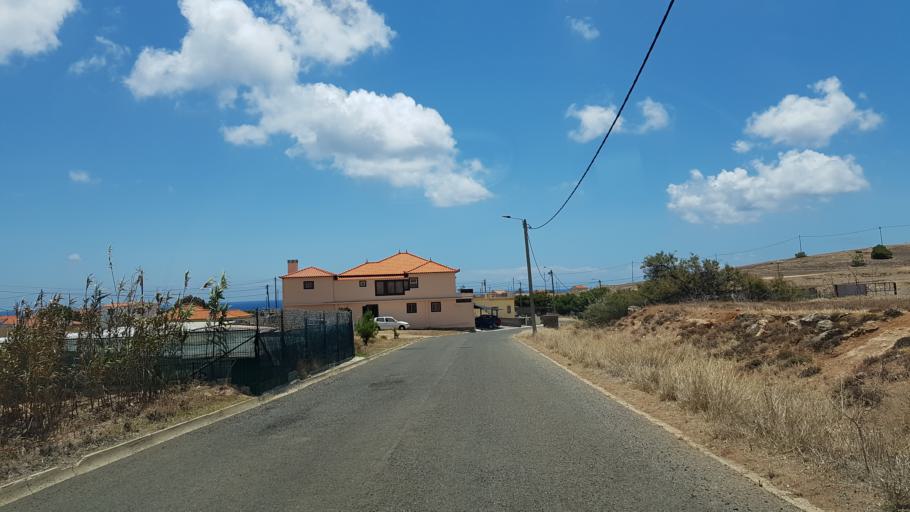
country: PT
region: Madeira
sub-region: Porto Santo
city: Vila de Porto Santo
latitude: 33.0624
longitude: -16.3607
